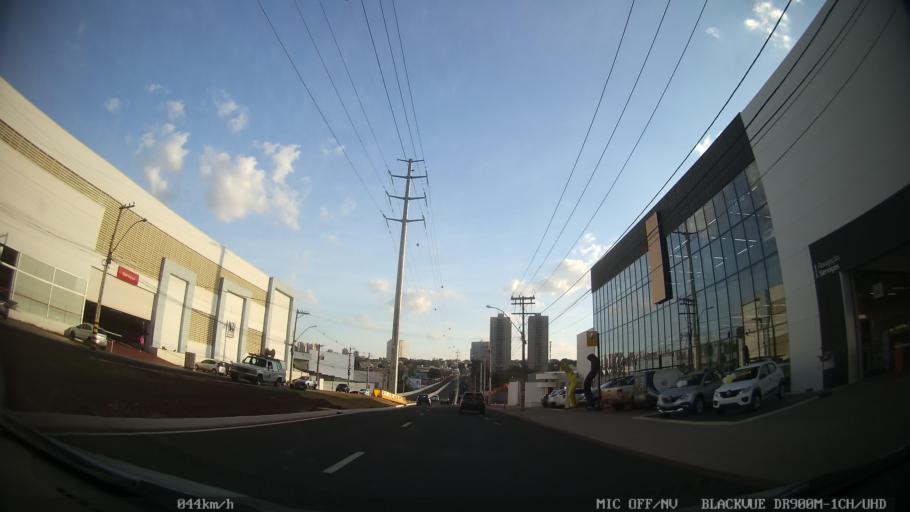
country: BR
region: Sao Paulo
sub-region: Ribeirao Preto
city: Ribeirao Preto
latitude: -21.1909
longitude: -47.7957
